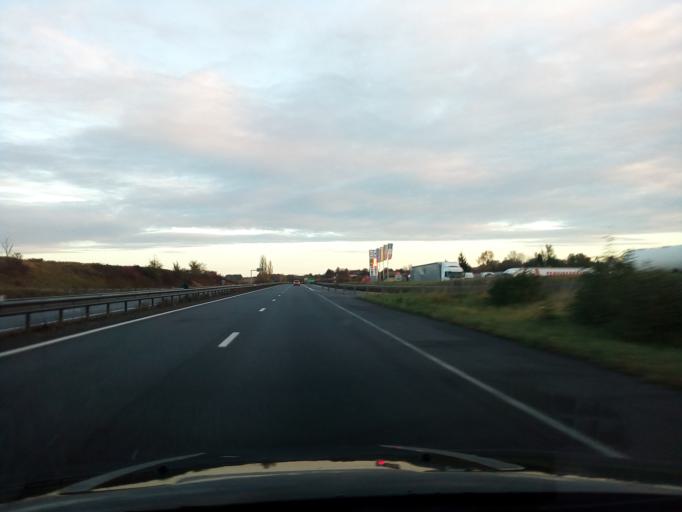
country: FR
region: Poitou-Charentes
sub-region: Departement de la Charente-Maritime
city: Chevanceaux
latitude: 45.2935
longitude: -0.2406
